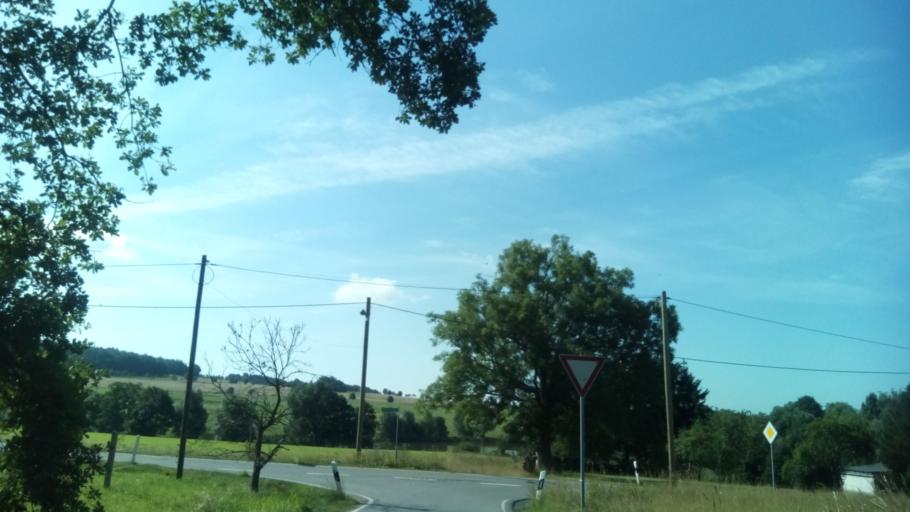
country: DE
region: Saxony
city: Niederschona
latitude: 50.9788
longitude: 13.4196
